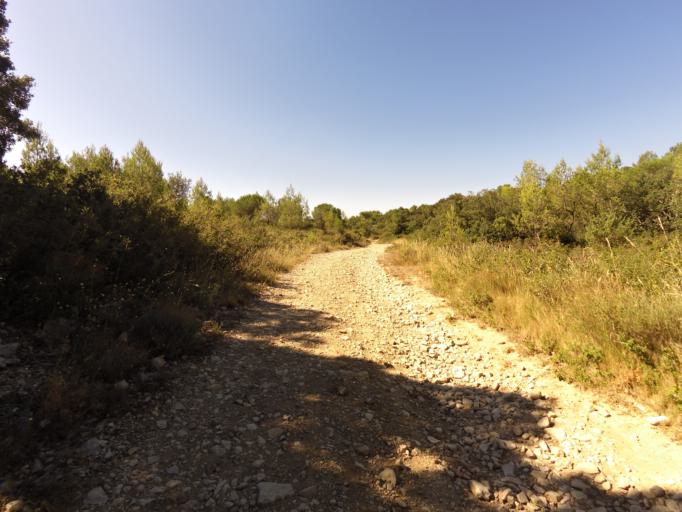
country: FR
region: Languedoc-Roussillon
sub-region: Departement du Gard
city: Congenies
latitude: 43.7609
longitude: 4.1767
